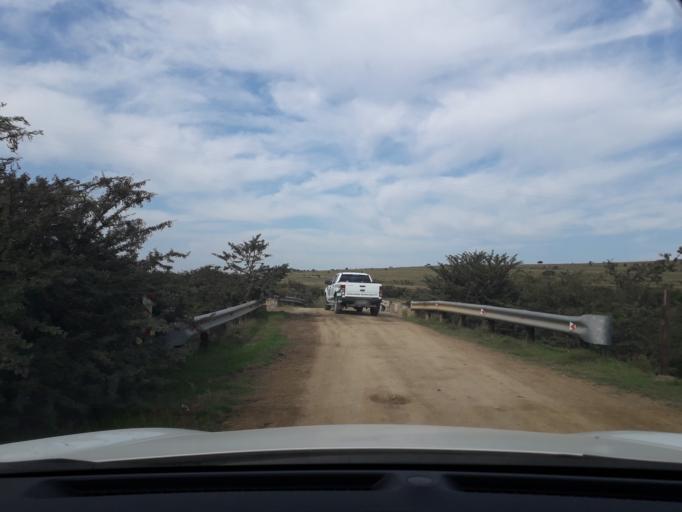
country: ZA
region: Eastern Cape
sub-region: Buffalo City Metropolitan Municipality
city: Bhisho
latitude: -32.9952
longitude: 27.3372
